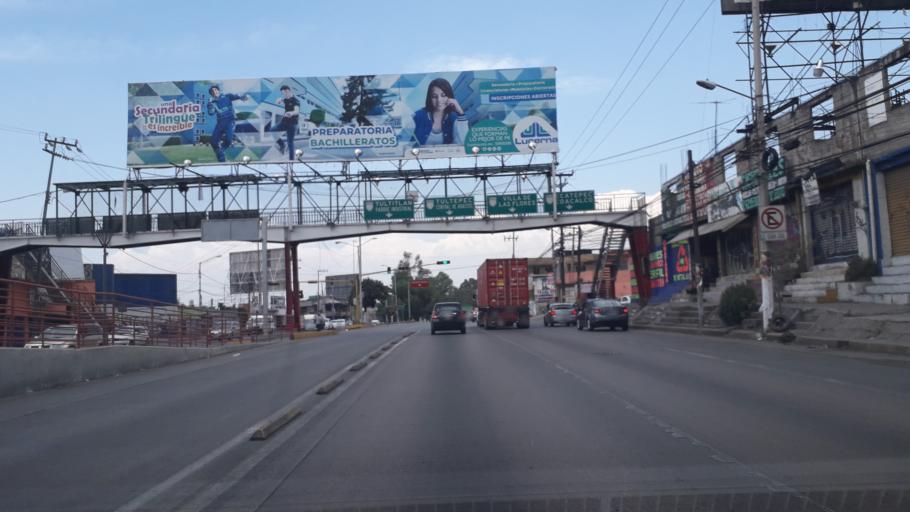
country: MX
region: Mexico
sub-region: Tultitlan
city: Buenavista
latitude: 19.6173
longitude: -99.1787
